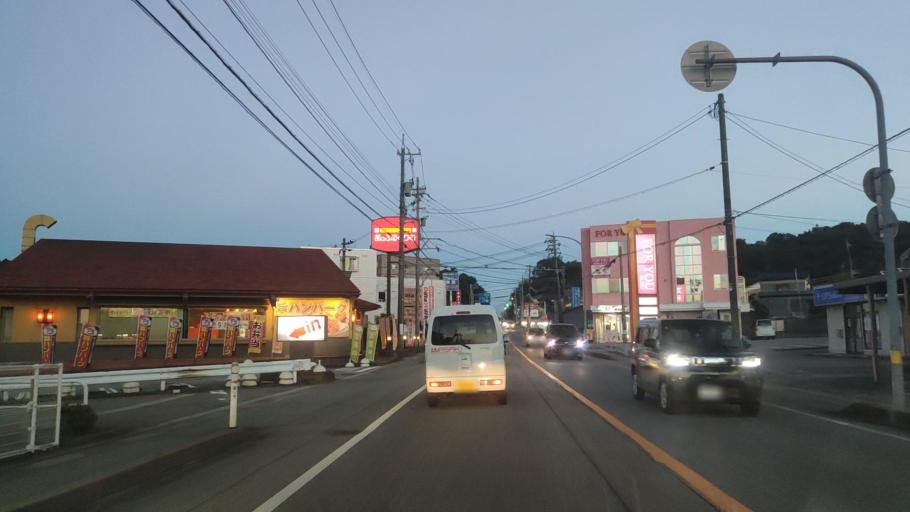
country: JP
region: Toyama
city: Toyama-shi
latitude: 36.7081
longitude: 137.1764
